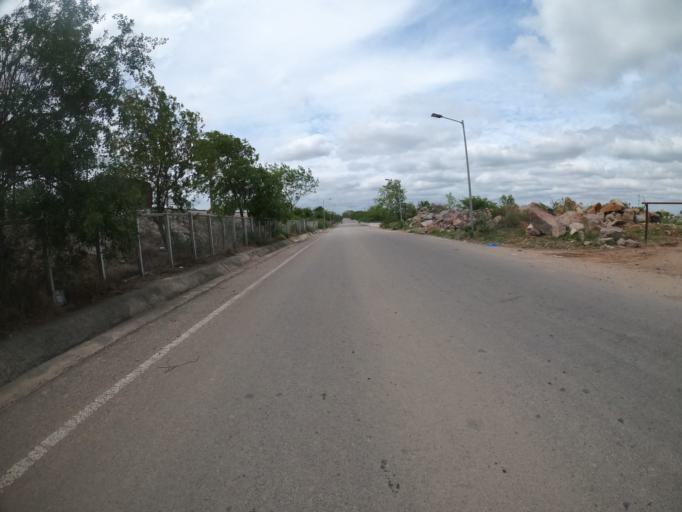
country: IN
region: Telangana
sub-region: Hyderabad
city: Hyderabad
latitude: 17.3048
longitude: 78.3778
